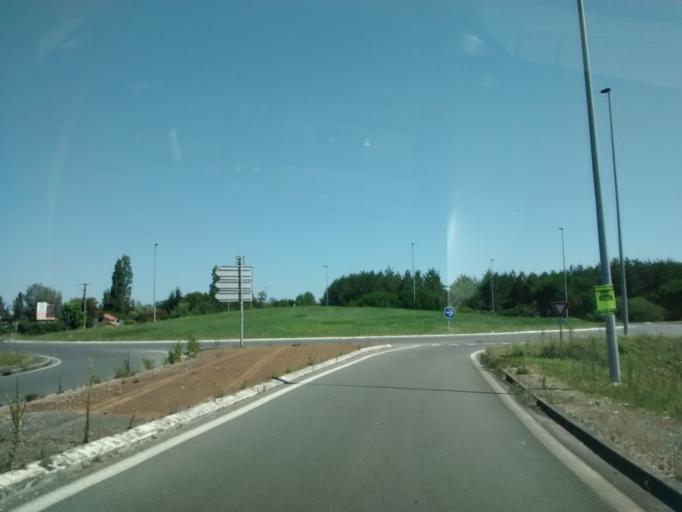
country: FR
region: Aquitaine
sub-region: Departement de la Gironde
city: Abzac
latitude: 45.0126
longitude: -0.1046
